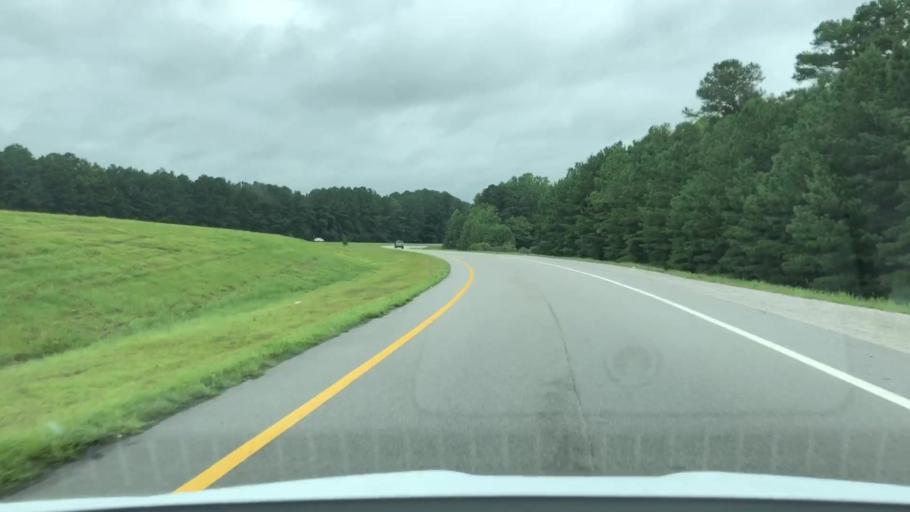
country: US
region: North Carolina
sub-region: Wilson County
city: Lucama
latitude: 35.7335
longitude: -78.0091
